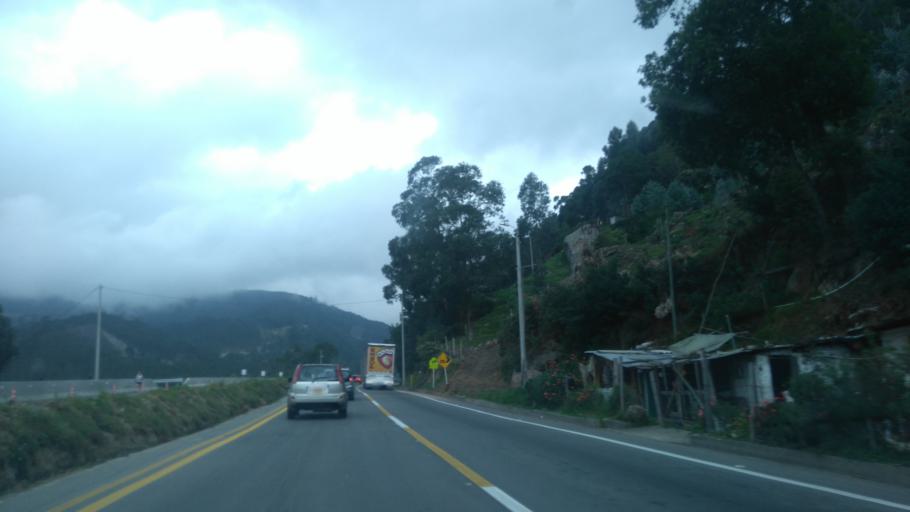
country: CO
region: Cundinamarca
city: El Rosal
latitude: 4.9066
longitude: -74.3043
